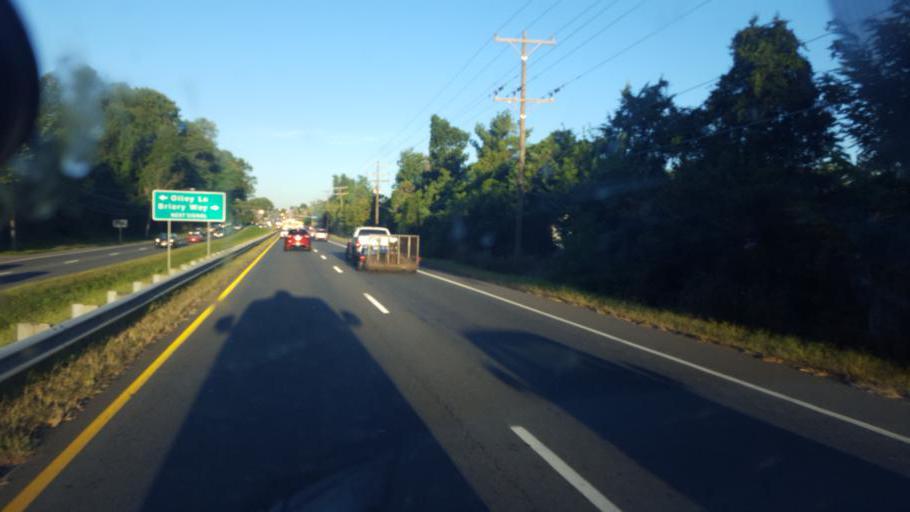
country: US
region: Virginia
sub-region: Fairfax County
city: Mantua
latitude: 38.8401
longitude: -77.2630
